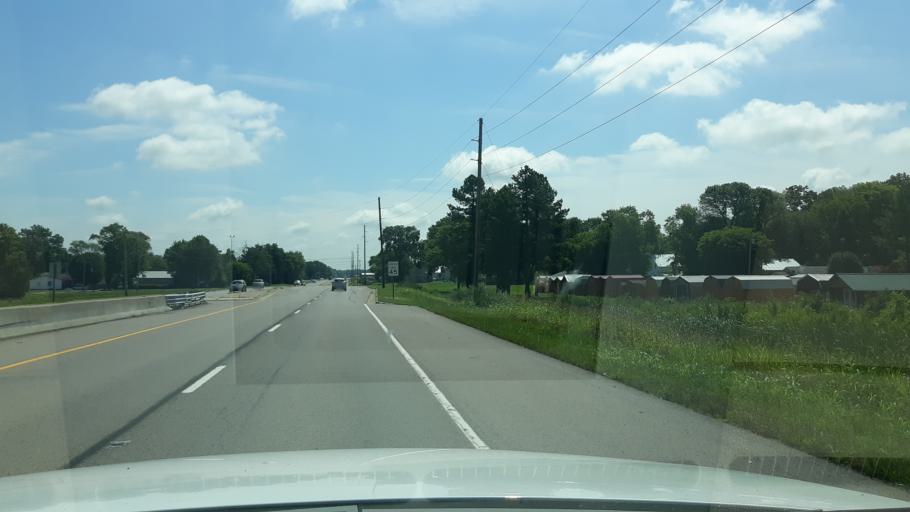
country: US
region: Illinois
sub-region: Saline County
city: Harrisburg
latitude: 37.7434
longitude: -88.5477
